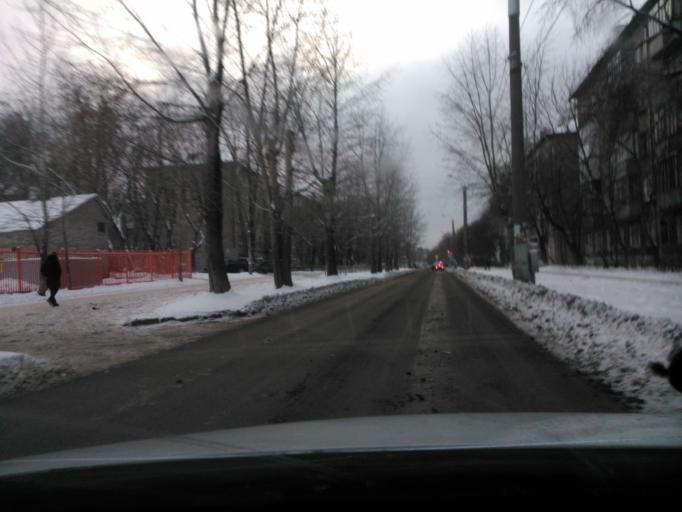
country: RU
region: Perm
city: Perm
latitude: 57.9871
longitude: 56.1967
